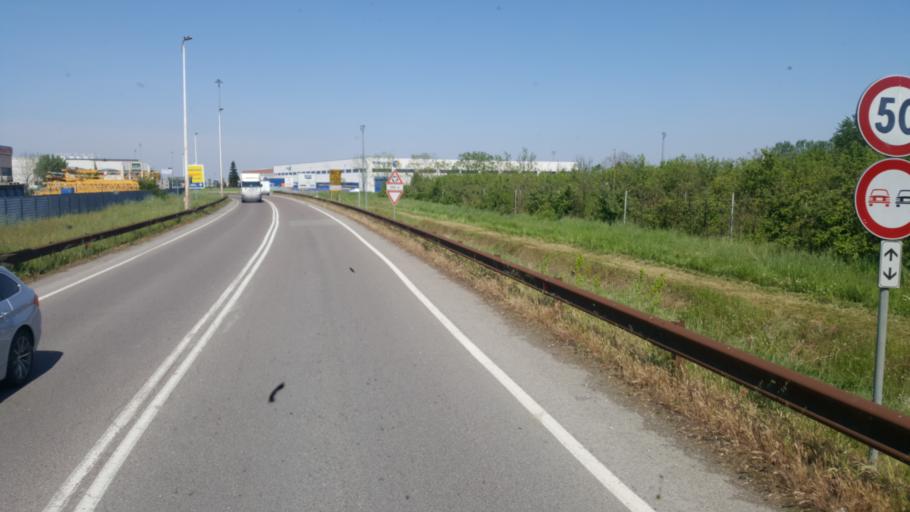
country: IT
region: Emilia-Romagna
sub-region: Provincia di Modena
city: Campogalliano
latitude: 44.6821
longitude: 10.8567
